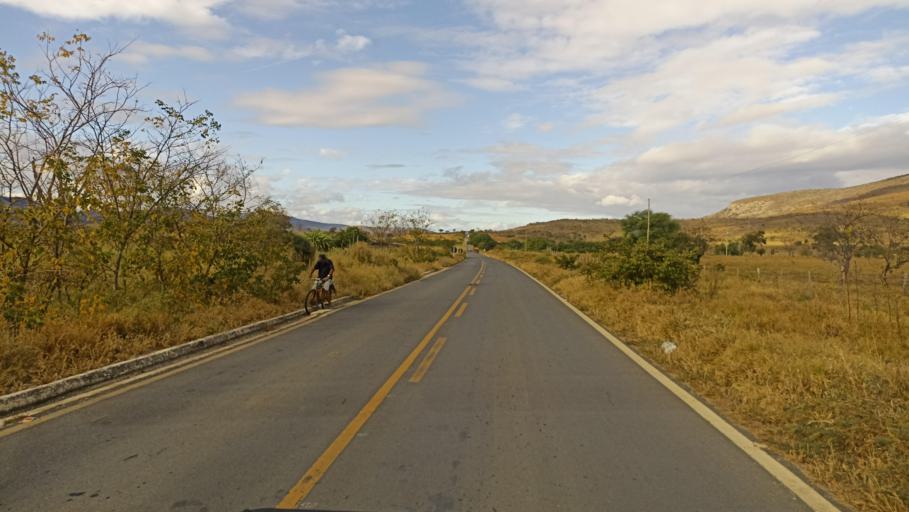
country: BR
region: Minas Gerais
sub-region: Itinga
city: Itinga
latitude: -16.5835
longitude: -41.6472
